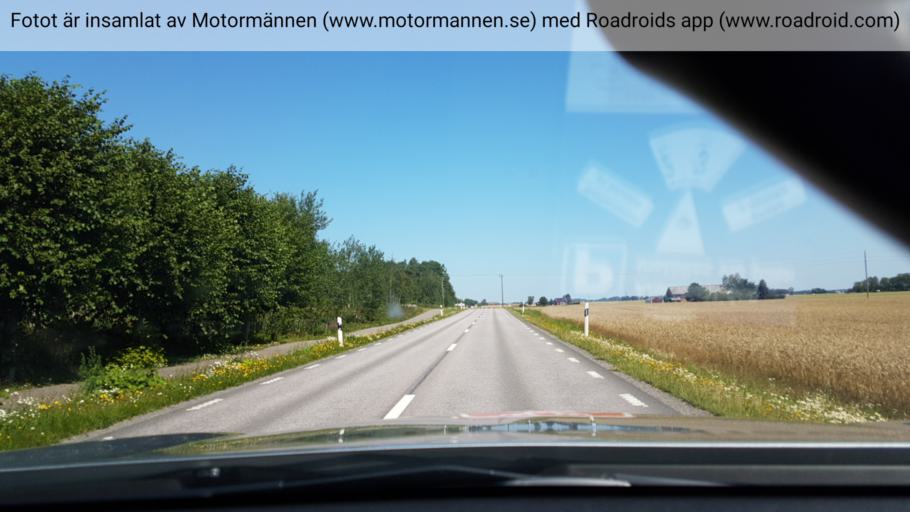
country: SE
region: Vaestra Goetaland
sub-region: Vara Kommun
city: Vara
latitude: 58.2812
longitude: 12.9567
